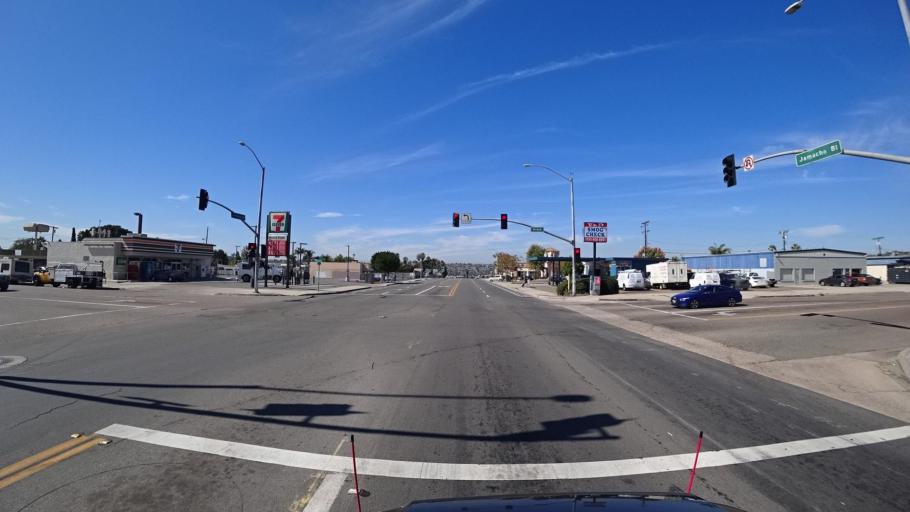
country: US
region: California
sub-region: San Diego County
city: La Presa
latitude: 32.7079
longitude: -116.9974
